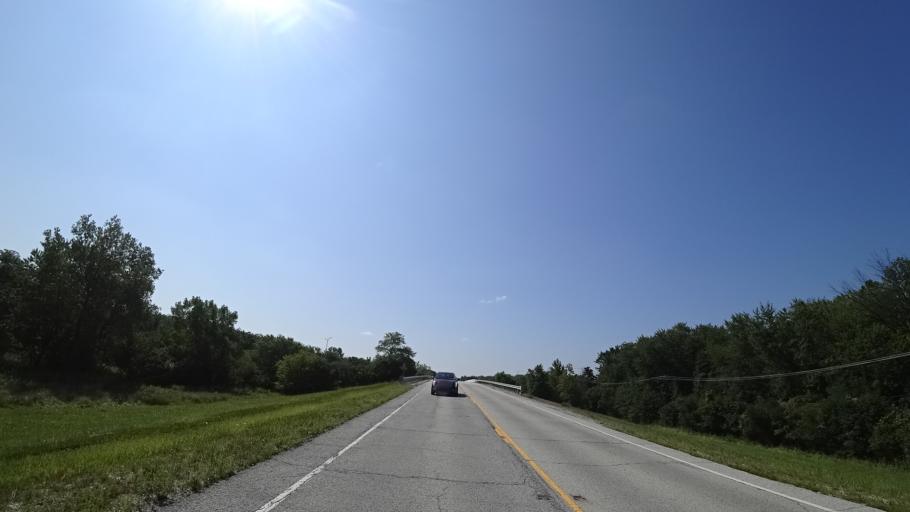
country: US
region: Illinois
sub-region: Cook County
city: Country Club Hills
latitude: 41.5629
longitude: -87.7525
